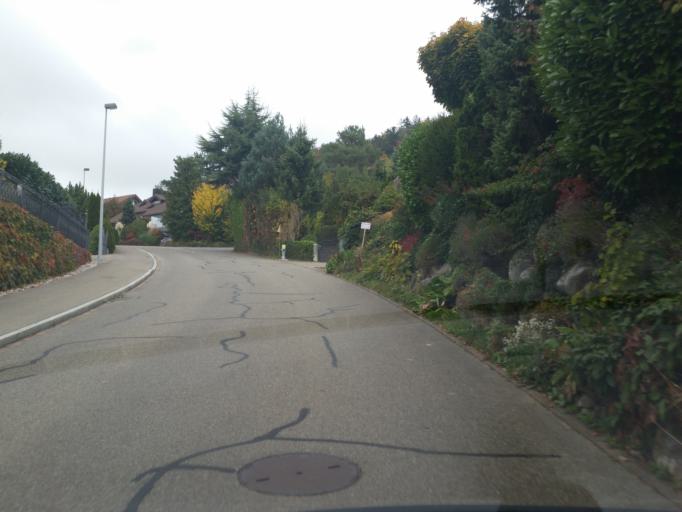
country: CH
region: Zurich
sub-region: Bezirk Dietikon
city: Geroldswil
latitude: 47.4188
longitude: 8.4187
